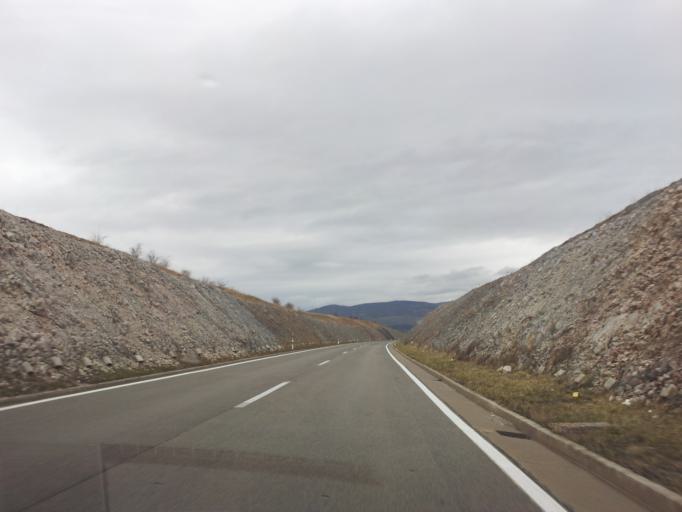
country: HR
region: Zadarska
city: Gracac
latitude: 44.5316
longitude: 15.7499
